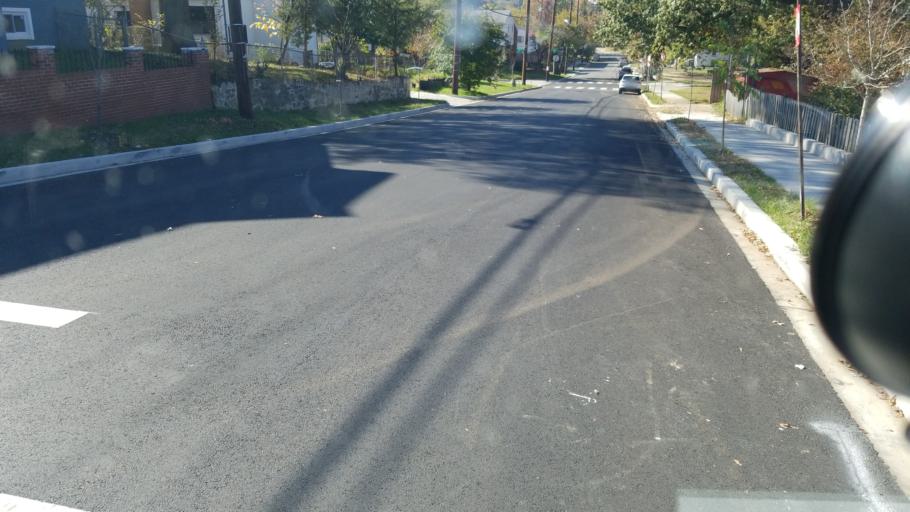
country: US
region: Maryland
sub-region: Prince George's County
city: Capitol Heights
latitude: 38.8909
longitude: -76.9301
